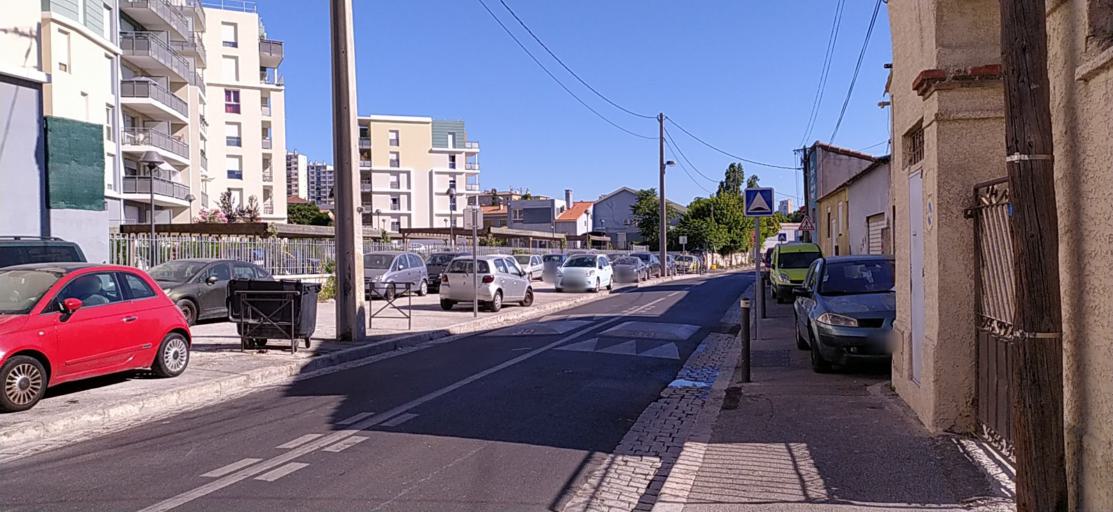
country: FR
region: Provence-Alpes-Cote d'Azur
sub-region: Departement des Bouches-du-Rhone
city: Marseille 14
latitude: 43.3397
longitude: 5.3626
